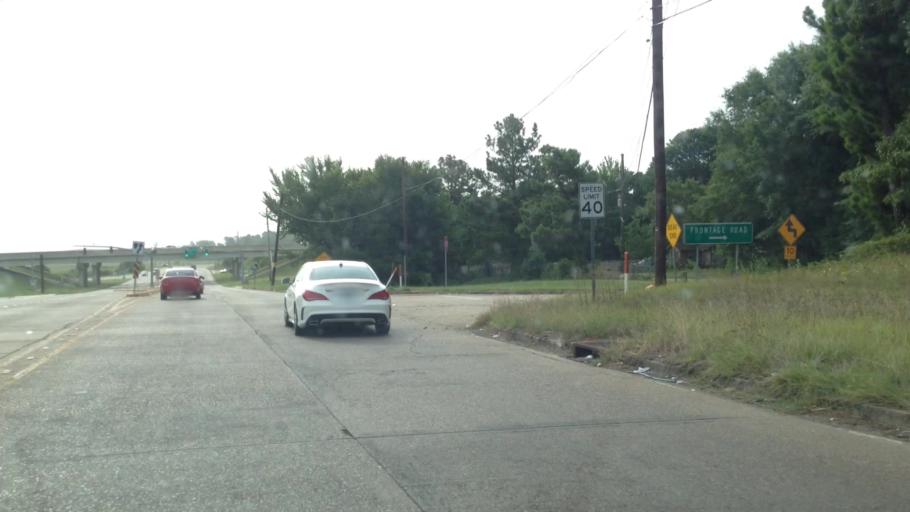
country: US
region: Louisiana
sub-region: Caddo Parish
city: Shreveport
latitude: 32.4421
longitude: -93.8446
